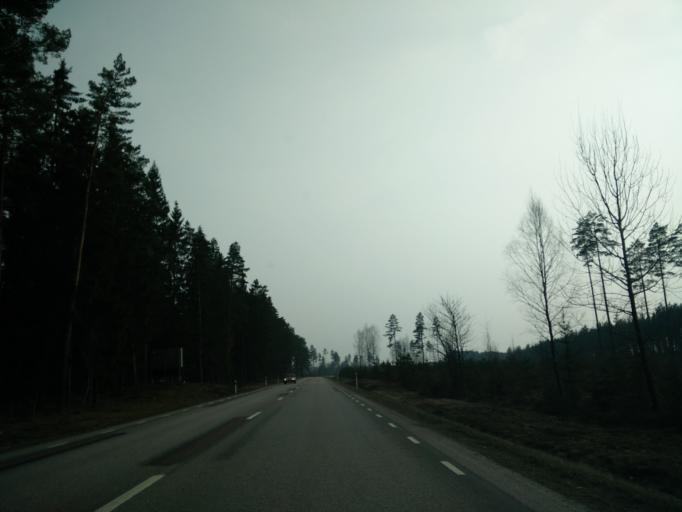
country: SE
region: Vaermland
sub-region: Forshaga Kommun
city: Forshaga
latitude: 59.5028
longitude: 13.4346
